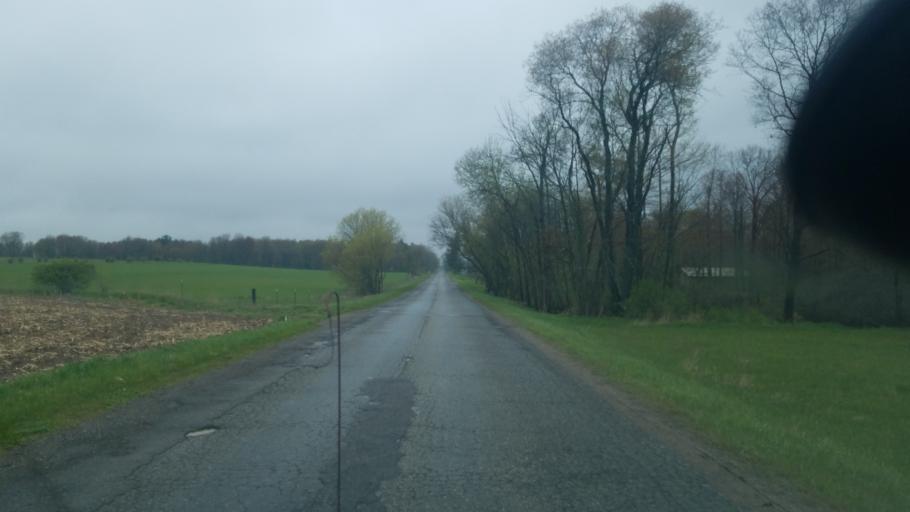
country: US
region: Michigan
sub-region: Mecosta County
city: Canadian Lakes
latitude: 43.5577
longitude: -85.3438
